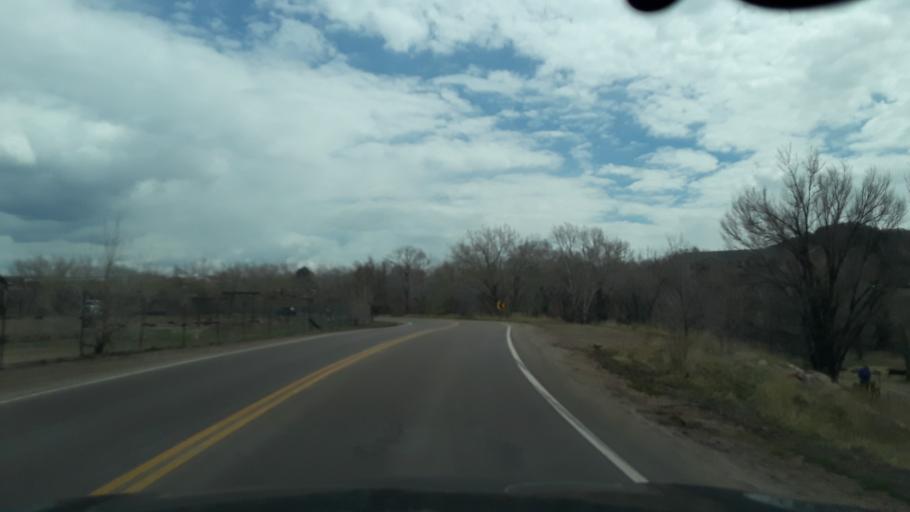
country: US
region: Colorado
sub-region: El Paso County
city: Air Force Academy
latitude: 38.9249
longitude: -104.8177
